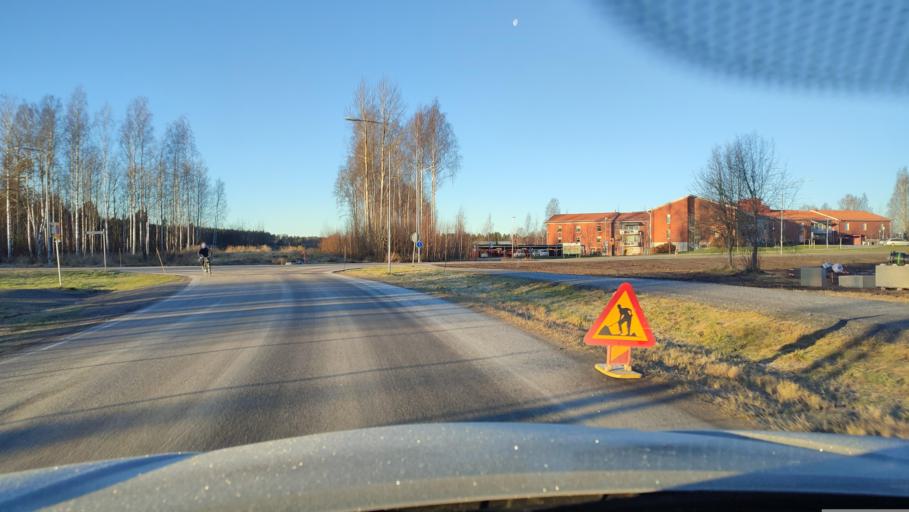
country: SE
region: Vaesterbotten
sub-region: Skelleftea Kommun
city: Skelleftea
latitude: 64.7407
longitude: 20.9434
